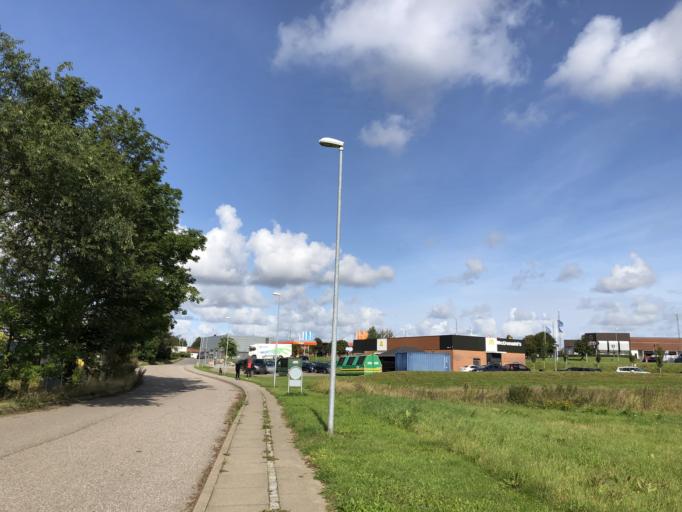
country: DK
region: South Denmark
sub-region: Vejle Kommune
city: Vejle
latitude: 55.6738
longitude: 9.5802
